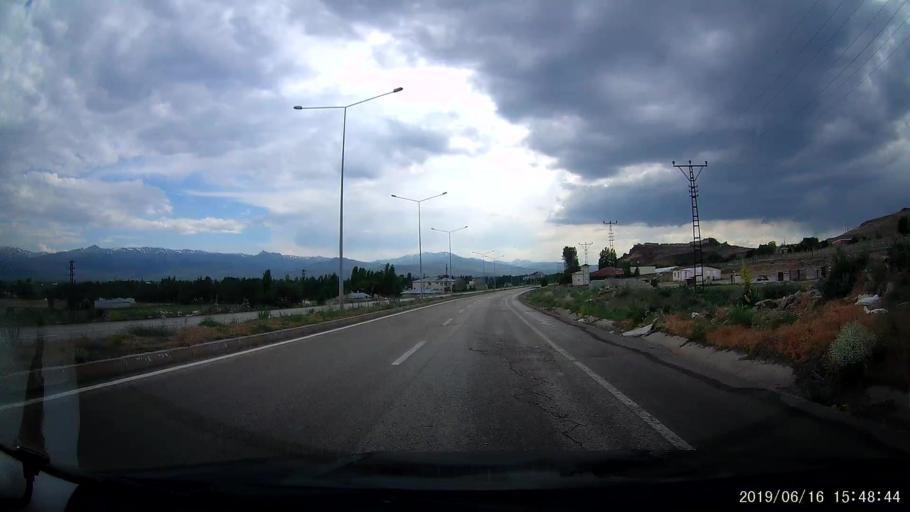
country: TR
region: Erzurum
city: Pasinler
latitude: 39.9808
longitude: 41.6963
